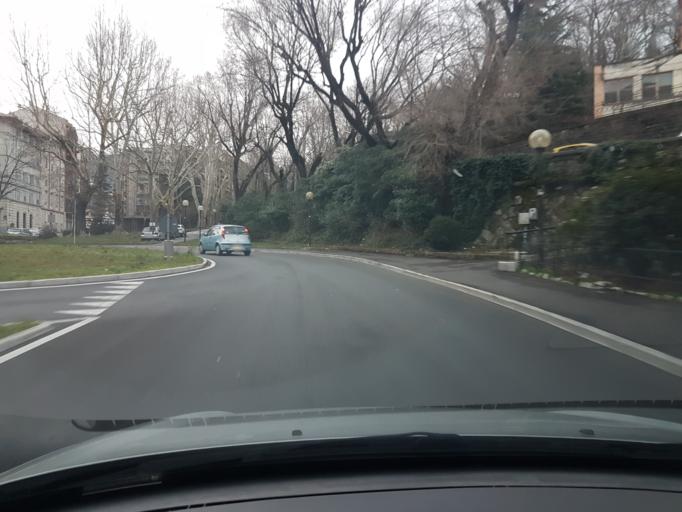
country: IT
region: Friuli Venezia Giulia
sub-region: Provincia di Trieste
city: Trieste
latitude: 45.6550
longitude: 13.7980
